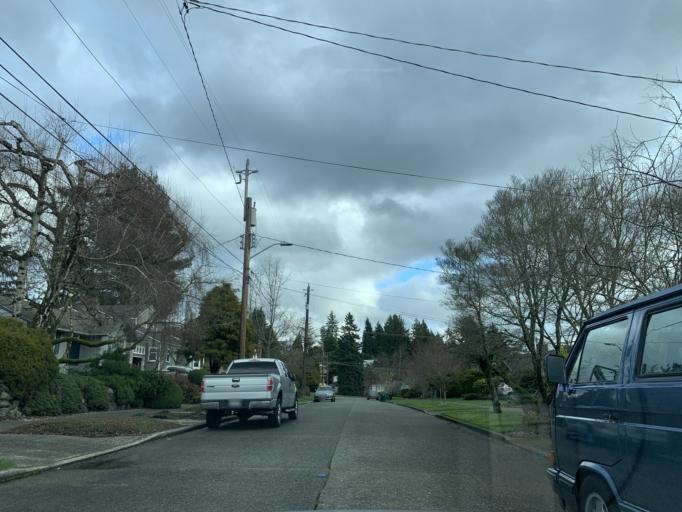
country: US
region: Washington
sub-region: King County
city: Yarrow Point
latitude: 47.6703
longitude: -122.2810
